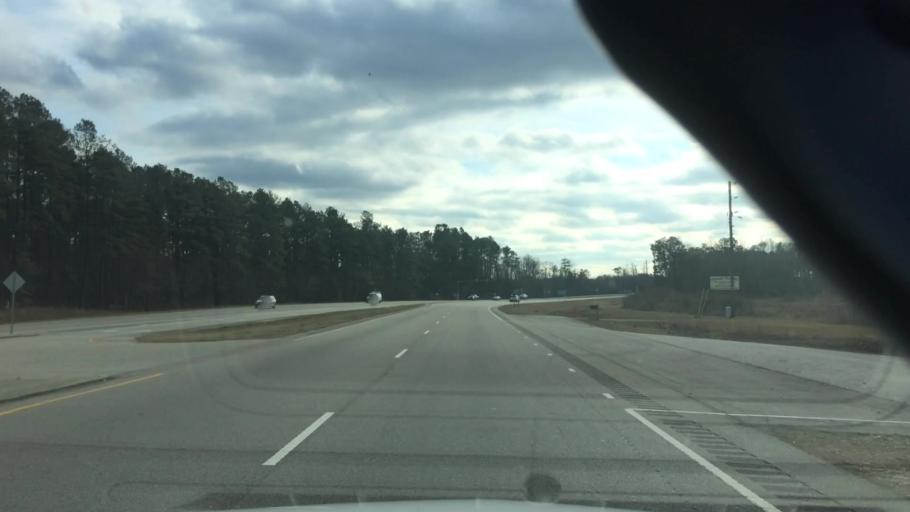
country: US
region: North Carolina
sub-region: Brunswick County
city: Bolivia
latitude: 34.1399
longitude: -78.0941
